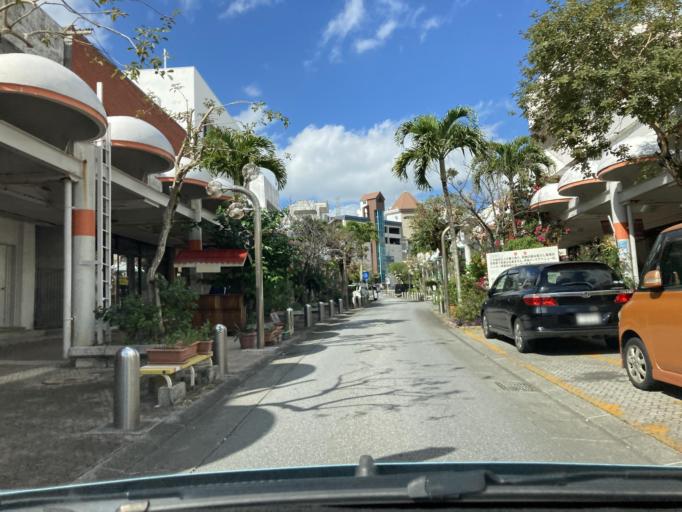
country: JP
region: Okinawa
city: Okinawa
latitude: 26.3395
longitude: 127.7998
